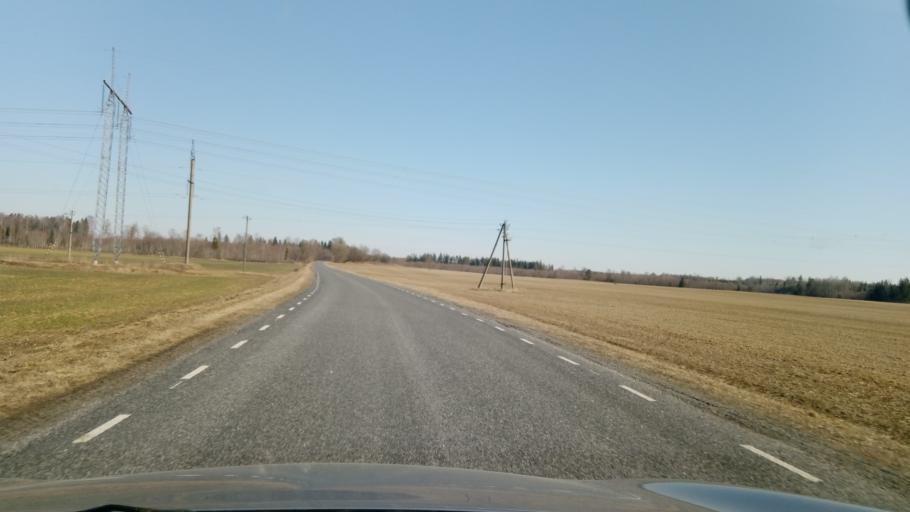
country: EE
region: Laeaene-Virumaa
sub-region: Tamsalu vald
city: Tamsalu
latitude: 59.1785
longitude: 26.1273
